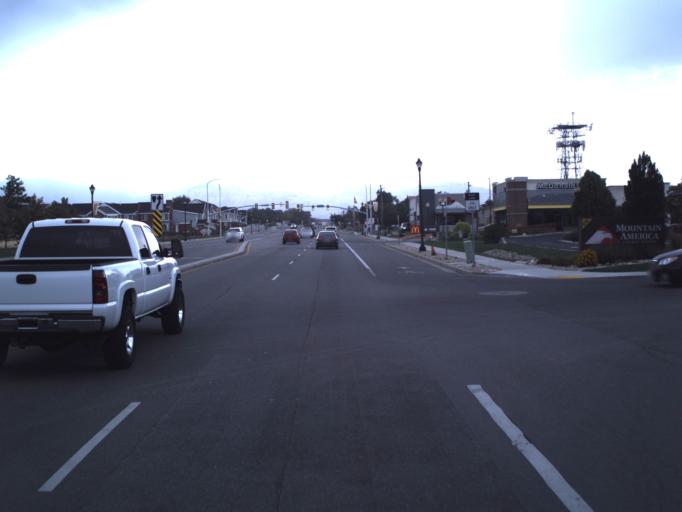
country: US
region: Utah
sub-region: Salt Lake County
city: Riverton
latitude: 40.5224
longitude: -111.9435
